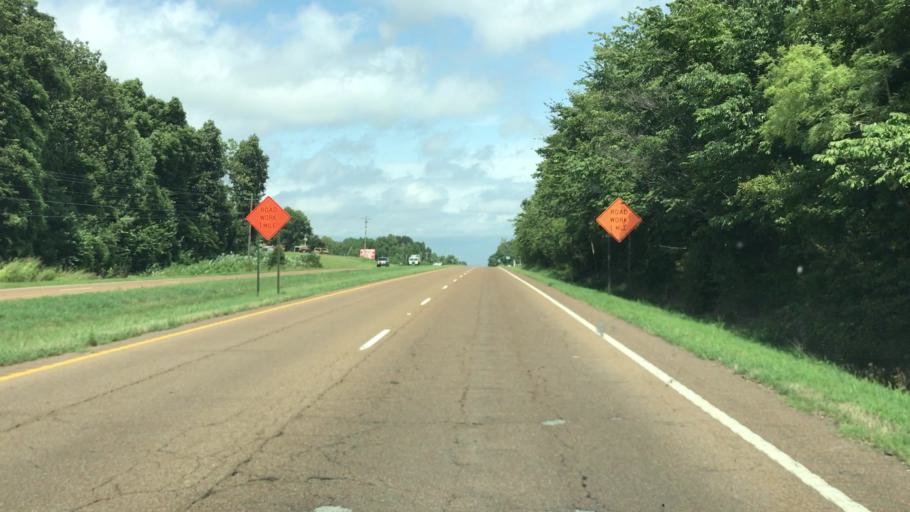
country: US
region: Tennessee
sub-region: Obion County
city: Englewood
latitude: 36.3731
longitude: -89.1199
